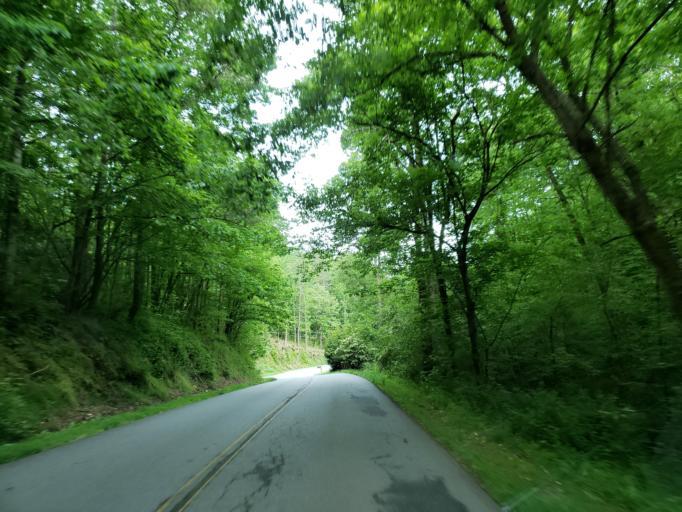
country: US
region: Georgia
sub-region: Fannin County
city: Blue Ridge
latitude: 34.8580
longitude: -84.3402
